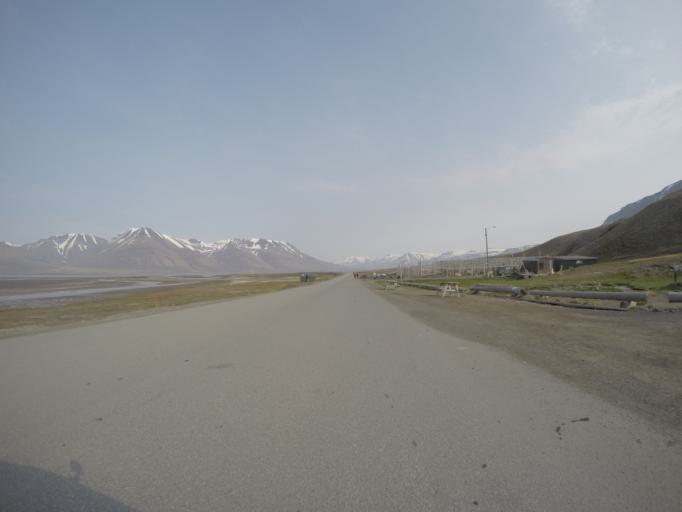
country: SJ
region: Svalbard
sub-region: Spitsbergen
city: Longyearbyen
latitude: 78.2183
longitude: 15.6991
